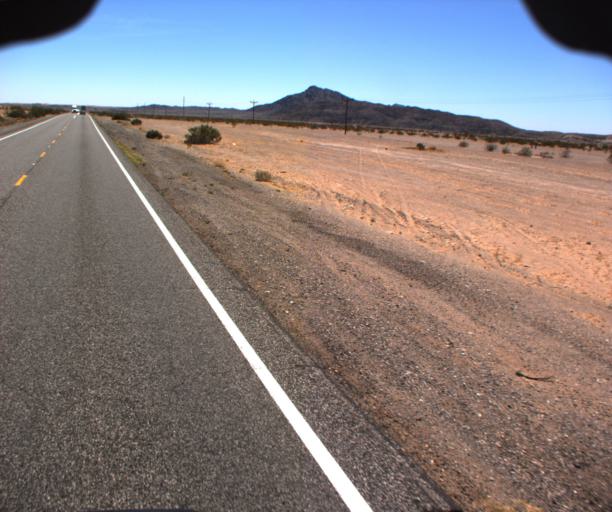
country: US
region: Arizona
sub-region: La Paz County
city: Parker
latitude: 34.0448
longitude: -114.2582
